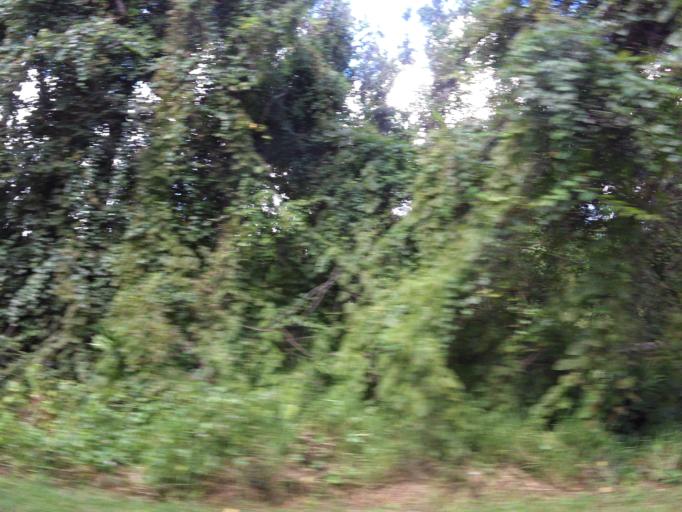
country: US
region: Florida
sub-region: Nassau County
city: Fernandina Beach
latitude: 30.5934
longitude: -81.4464
